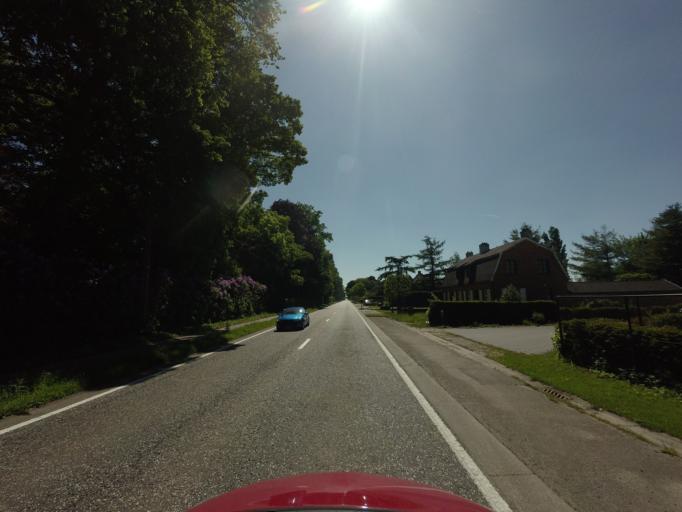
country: BE
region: Flanders
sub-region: Provincie Antwerpen
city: Ravels
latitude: 51.3510
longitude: 4.9834
